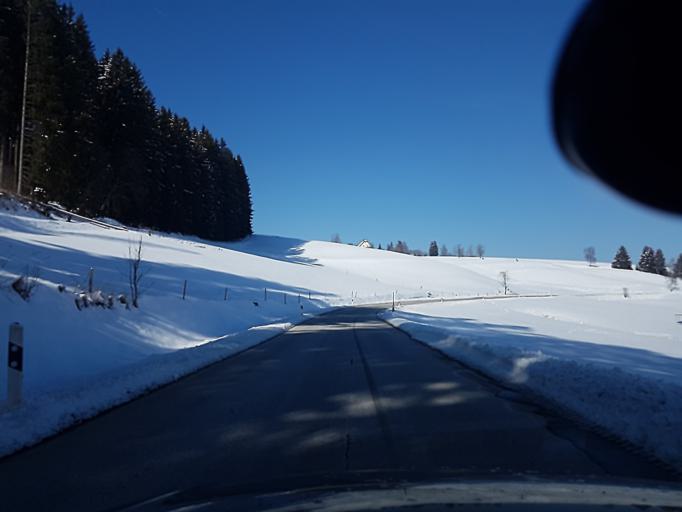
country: DE
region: Baden-Wuerttemberg
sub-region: Freiburg Region
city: Unterkirnach
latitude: 48.1060
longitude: 8.3931
